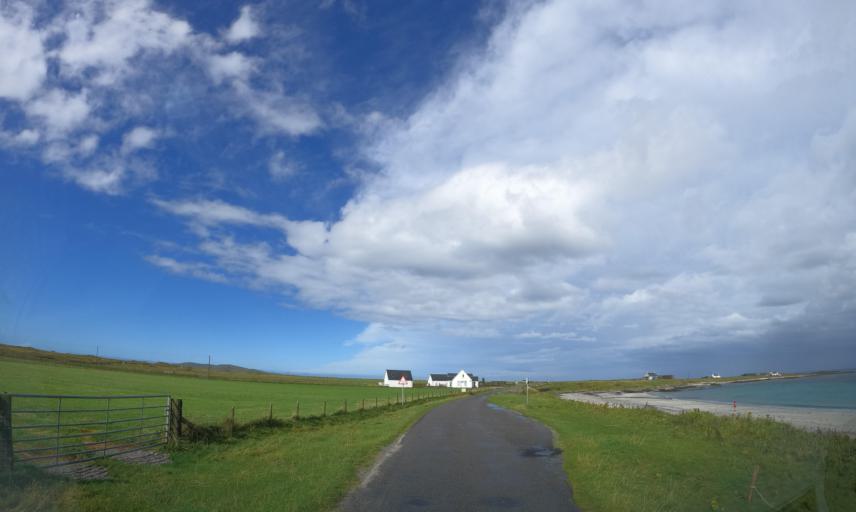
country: GB
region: Scotland
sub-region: Eilean Siar
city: Barra
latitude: 56.5183
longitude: -6.8847
